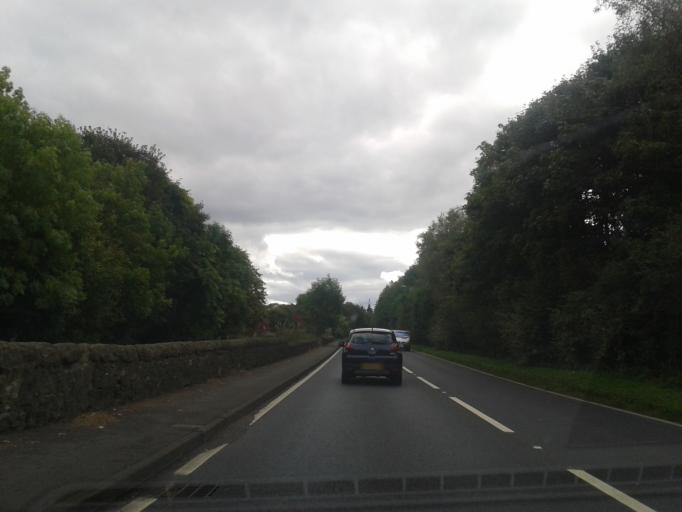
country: GB
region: Scotland
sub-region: Fife
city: Markinch
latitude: 56.2127
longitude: -3.1558
